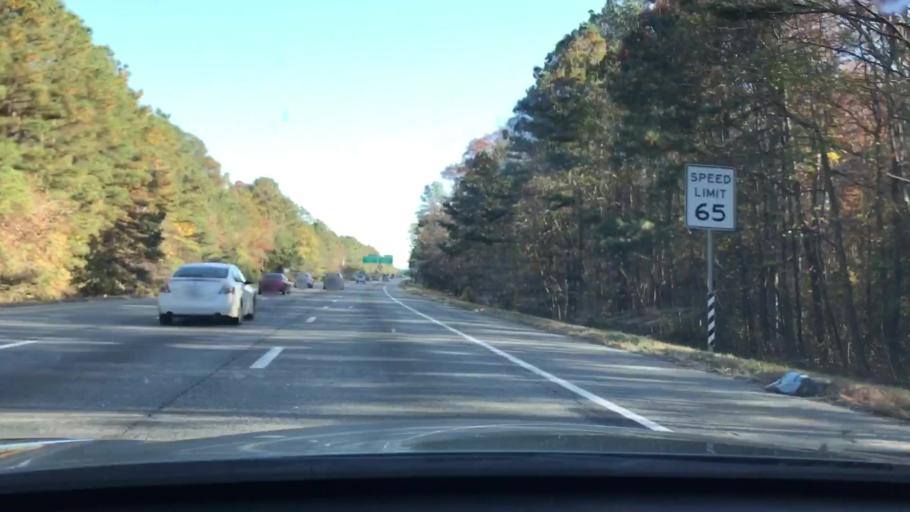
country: US
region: Virginia
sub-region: Henrico County
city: Glen Allen
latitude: 37.6740
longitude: -77.4970
